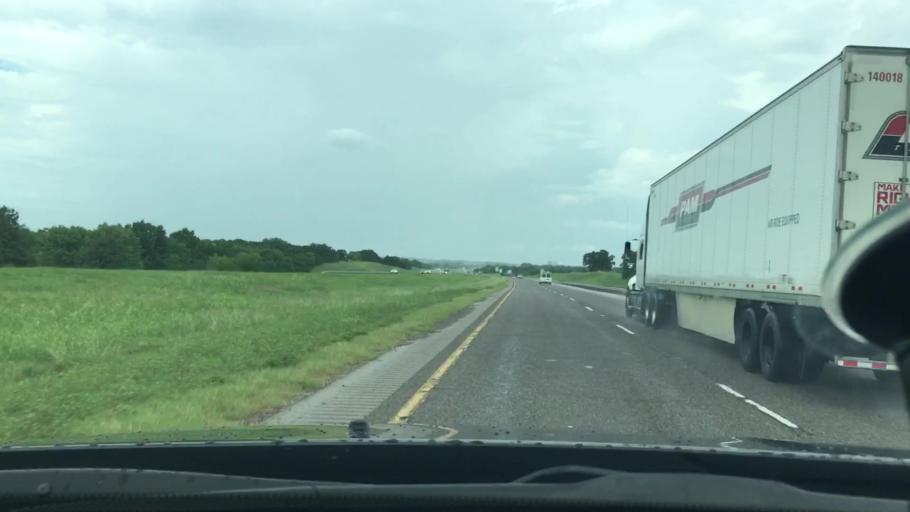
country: US
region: Oklahoma
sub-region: Garvin County
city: Wynnewood
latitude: 34.5834
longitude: -97.2027
